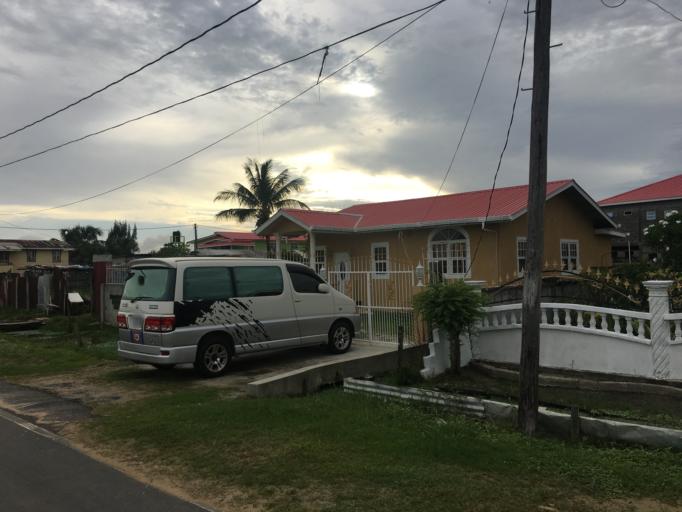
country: GY
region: Demerara-Mahaica
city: Georgetown
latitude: 6.8000
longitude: -58.1209
